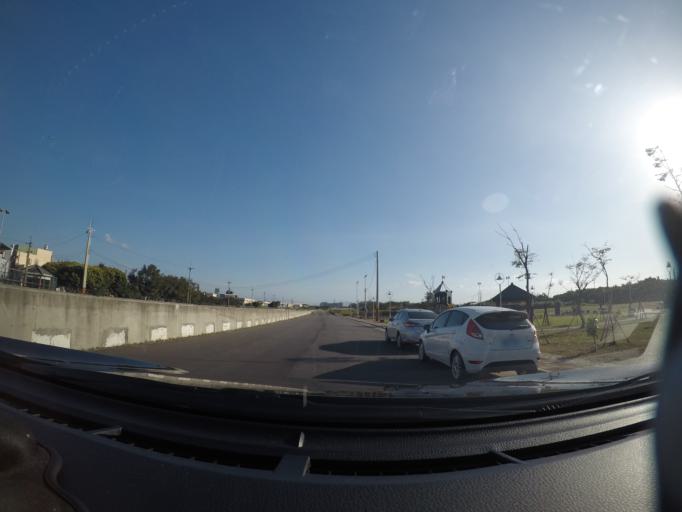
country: TW
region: Taiwan
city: Taoyuan City
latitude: 25.1078
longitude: 121.2538
